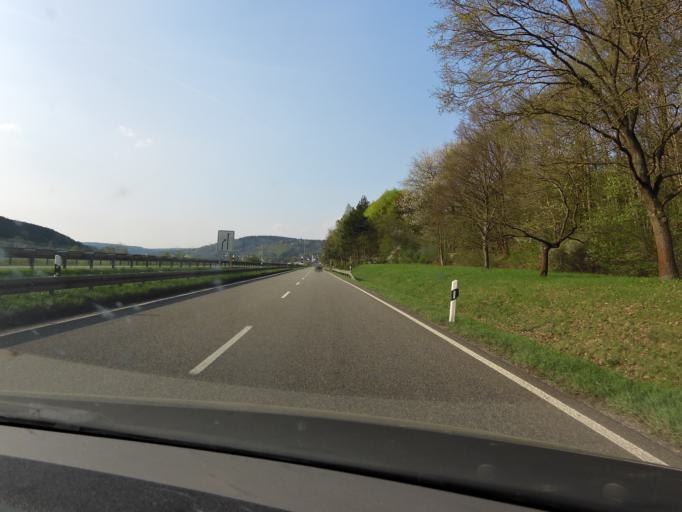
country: DE
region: Thuringia
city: Wasungen
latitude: 50.6458
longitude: 10.3807
